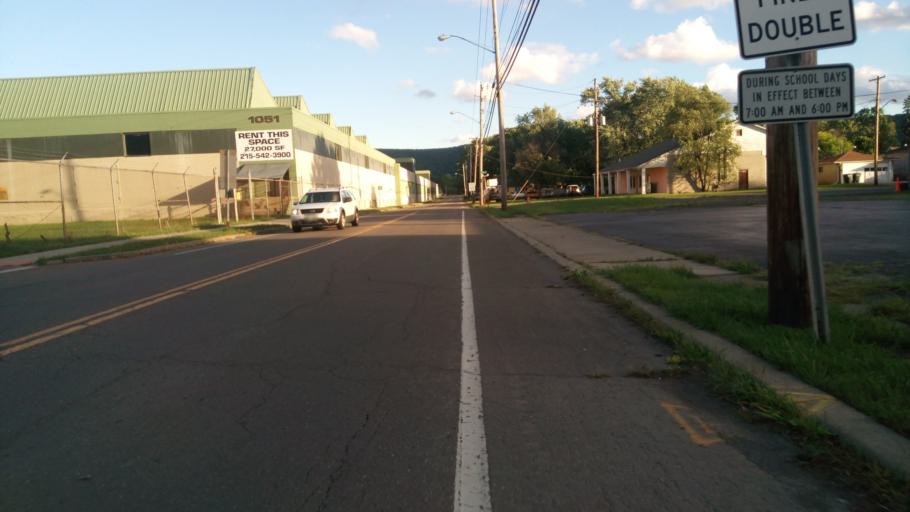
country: US
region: New York
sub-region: Chemung County
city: Elmira
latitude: 42.0678
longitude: -76.7976
